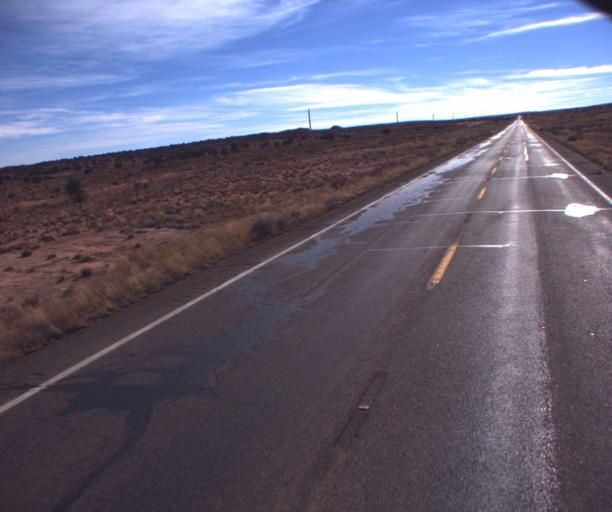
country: US
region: Arizona
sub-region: Coconino County
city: Kaibito
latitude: 36.6117
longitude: -111.1863
